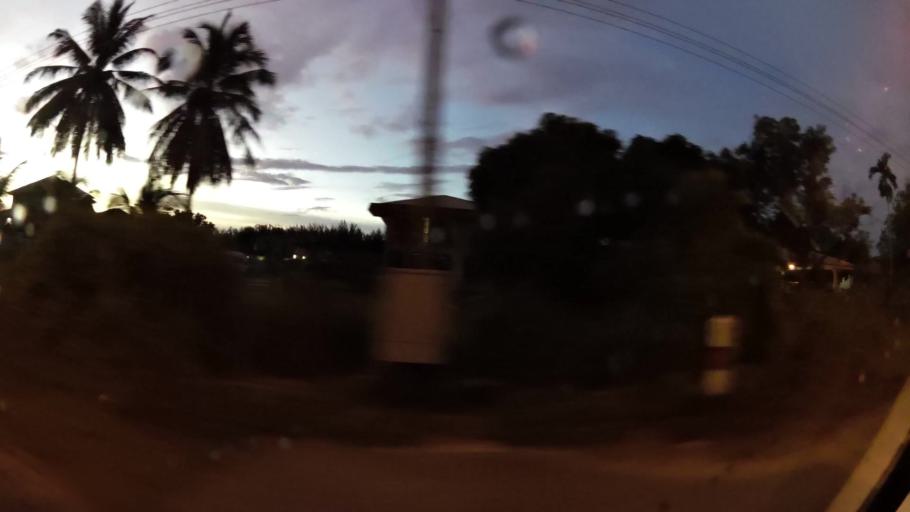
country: BN
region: Belait
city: Seria
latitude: 4.6565
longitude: 114.4359
